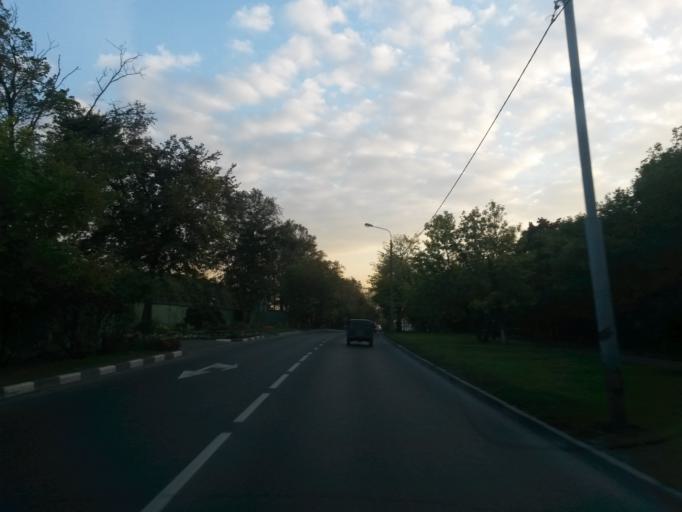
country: RU
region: Moscow
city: Orekhovo-Borisovo Severnoye
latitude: 55.6317
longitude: 37.6844
